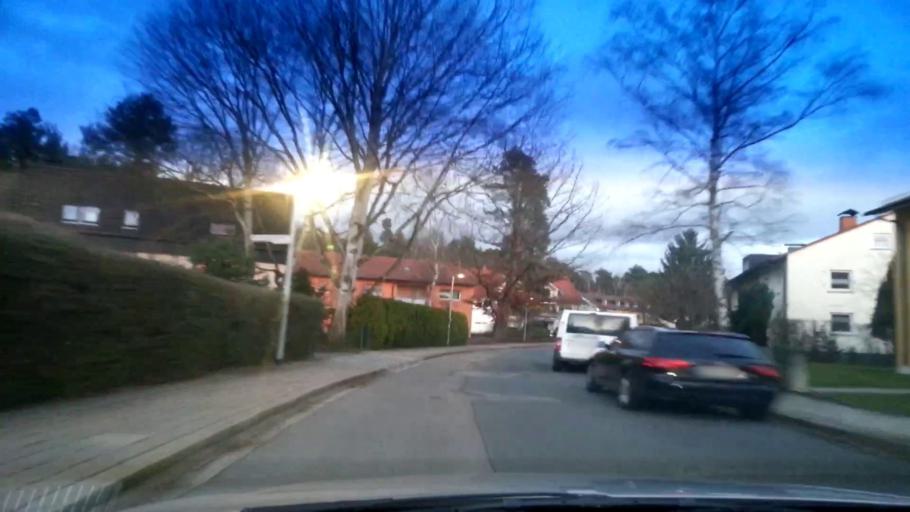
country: DE
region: Bavaria
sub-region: Upper Franconia
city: Gundelsheim
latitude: 49.9167
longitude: 10.9241
